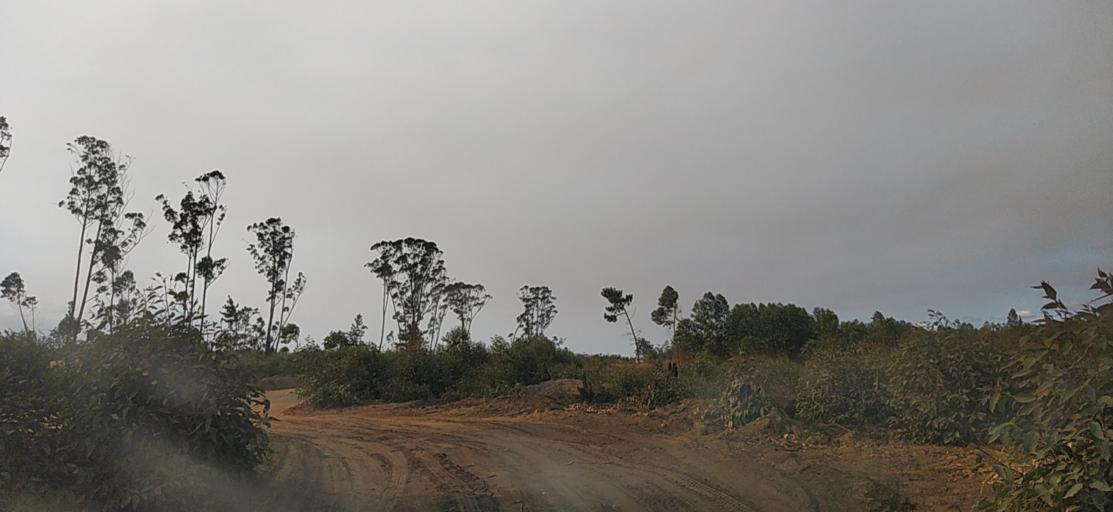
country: MG
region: Alaotra Mangoro
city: Moramanga
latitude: -18.6203
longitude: 48.2767
